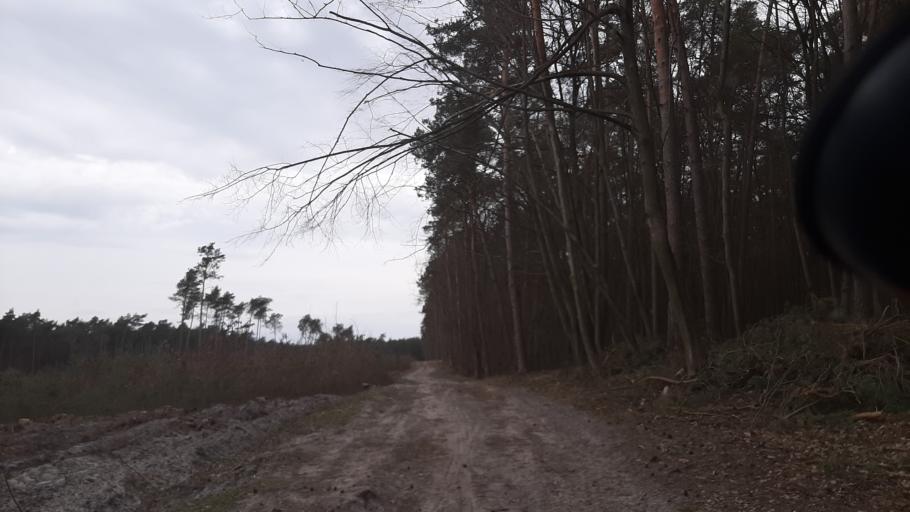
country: PL
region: Lublin Voivodeship
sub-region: Powiat lubelski
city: Garbow
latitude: 51.3945
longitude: 22.3790
